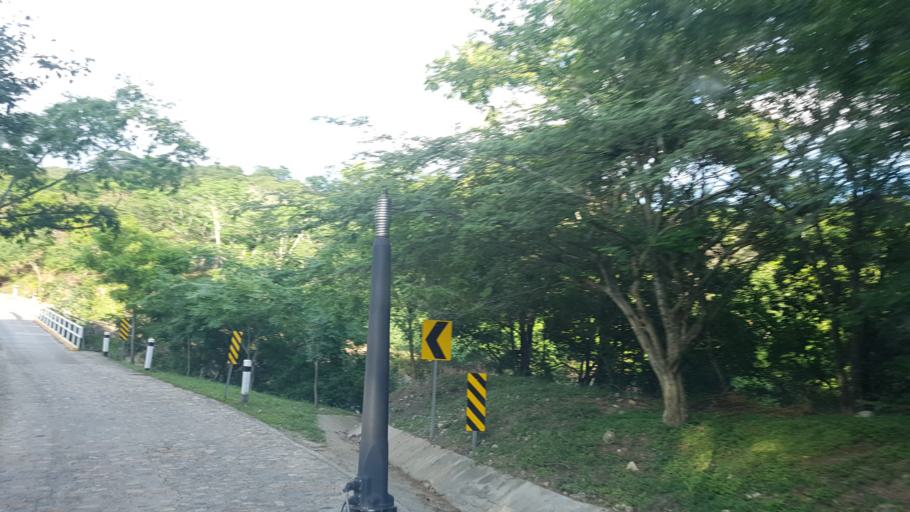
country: NI
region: Nueva Segovia
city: Ocotal
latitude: 13.6411
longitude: -86.5905
